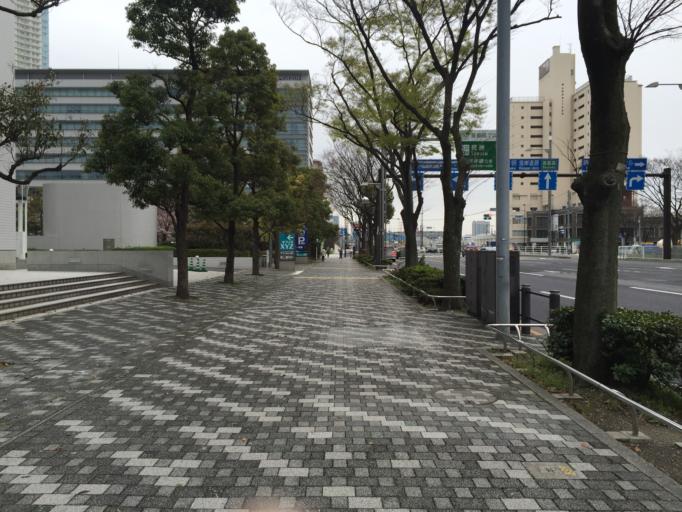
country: JP
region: Tokyo
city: Tokyo
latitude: 35.6563
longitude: 139.7810
